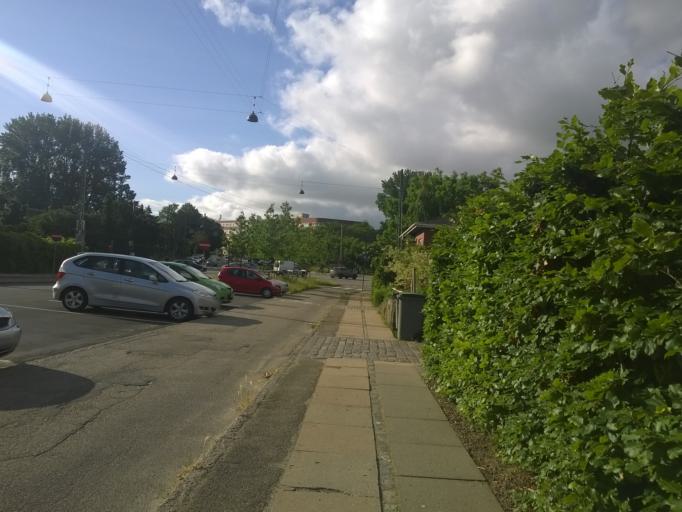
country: DK
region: Capital Region
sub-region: Kobenhavn
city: Vanlose
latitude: 55.6886
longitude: 12.5005
